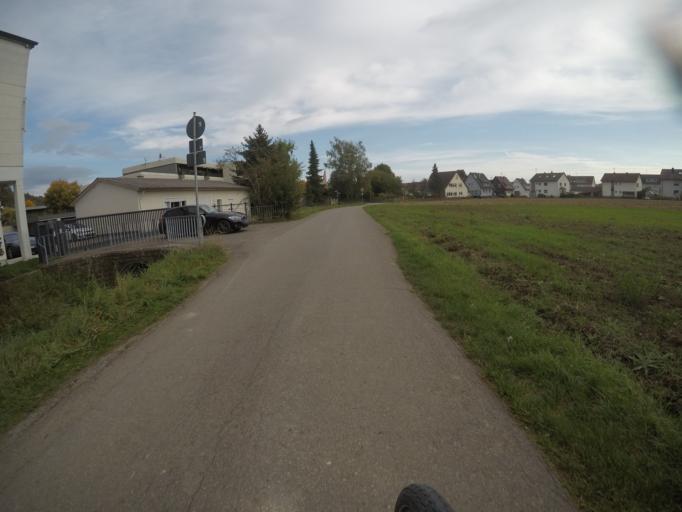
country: DE
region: Baden-Wuerttemberg
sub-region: Tuebingen Region
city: Rottenburg
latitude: 48.5339
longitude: 8.9610
